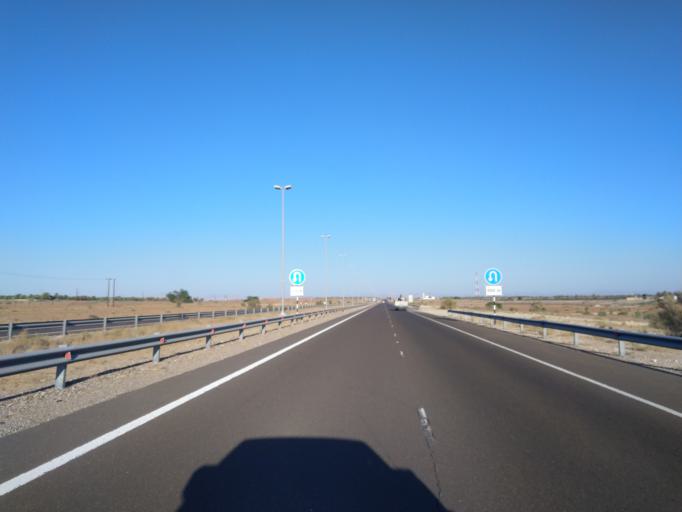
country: OM
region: Al Buraimi
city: Al Buraymi
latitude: 24.5393
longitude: 55.6202
